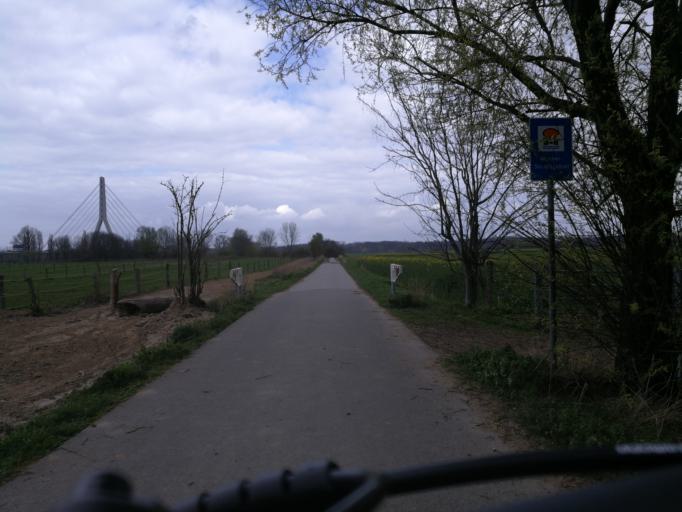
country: DE
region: North Rhine-Westphalia
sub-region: Regierungsbezirk Dusseldorf
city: Dusseldorf
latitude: 51.1754
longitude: 6.7792
